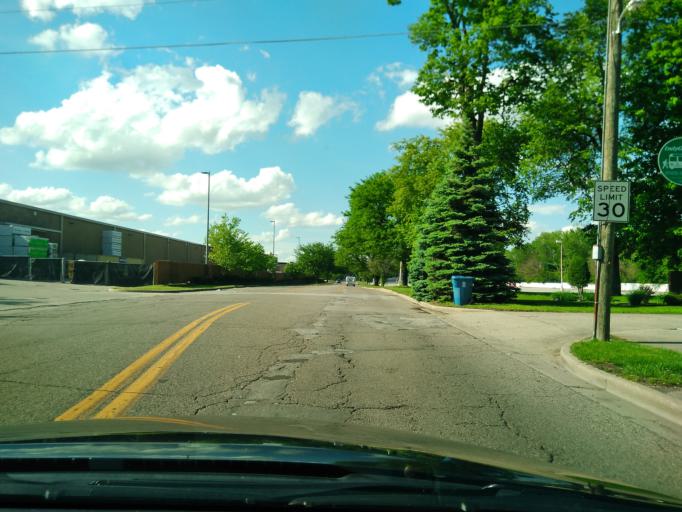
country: US
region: Indiana
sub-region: Marion County
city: Broad Ripple
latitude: 39.8630
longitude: -86.1175
